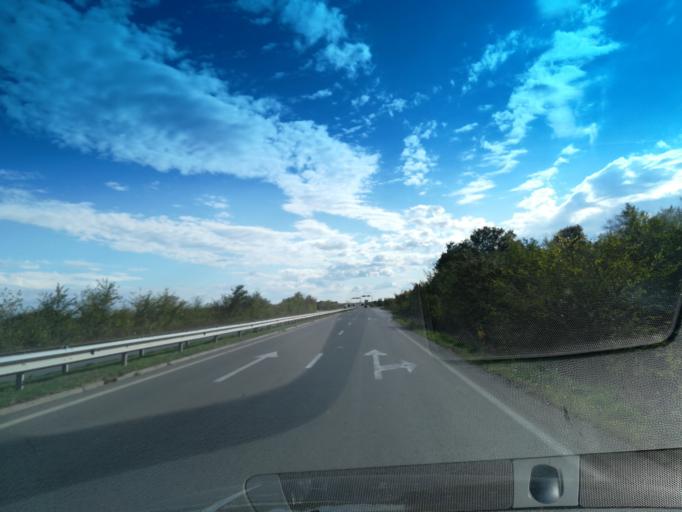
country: BG
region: Stara Zagora
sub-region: Obshtina Stara Zagora
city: Stara Zagora
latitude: 42.3447
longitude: 25.6603
